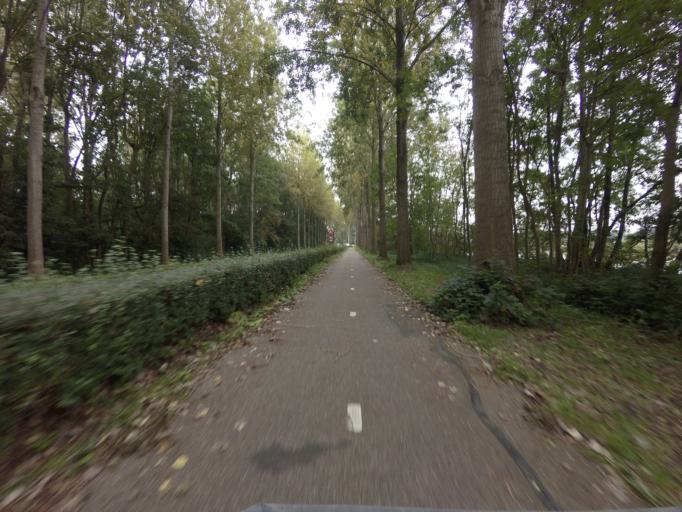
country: NL
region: Utrecht
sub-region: Stichtse Vecht
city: Vreeland
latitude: 52.2018
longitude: 5.0383
